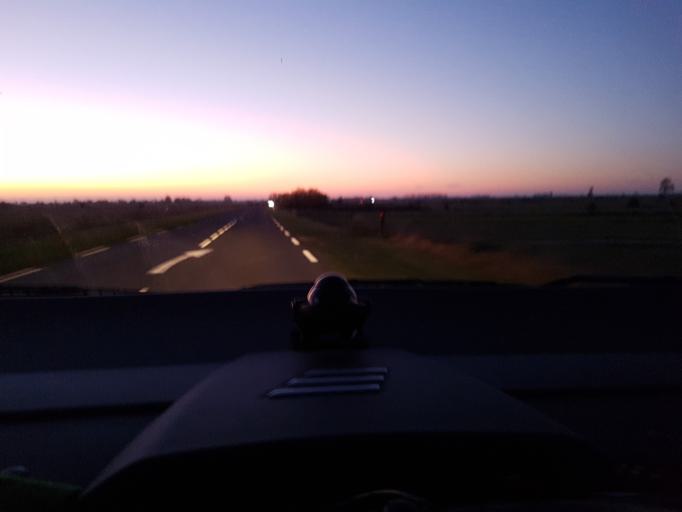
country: FR
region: Picardie
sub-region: Departement de la Somme
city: Pende
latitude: 50.1849
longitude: 1.5840
